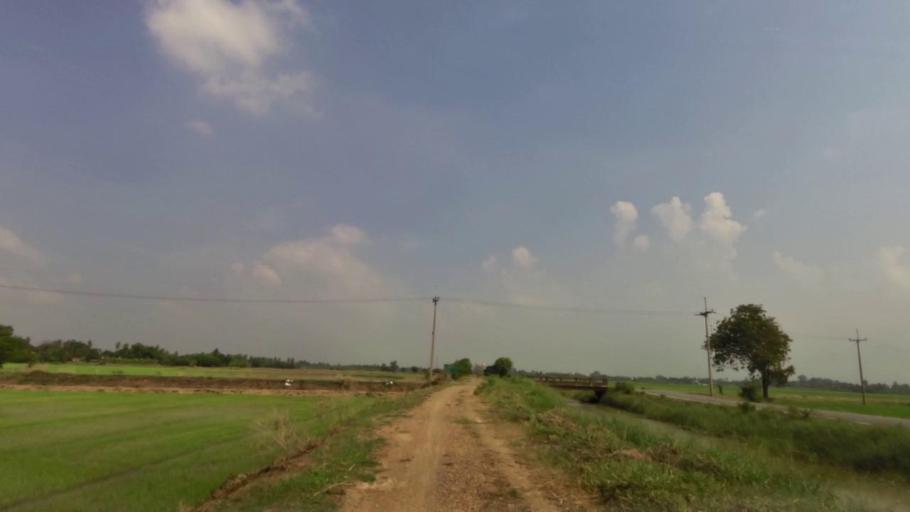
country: TH
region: Ang Thong
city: Pho Thong
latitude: 14.6188
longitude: 100.4018
